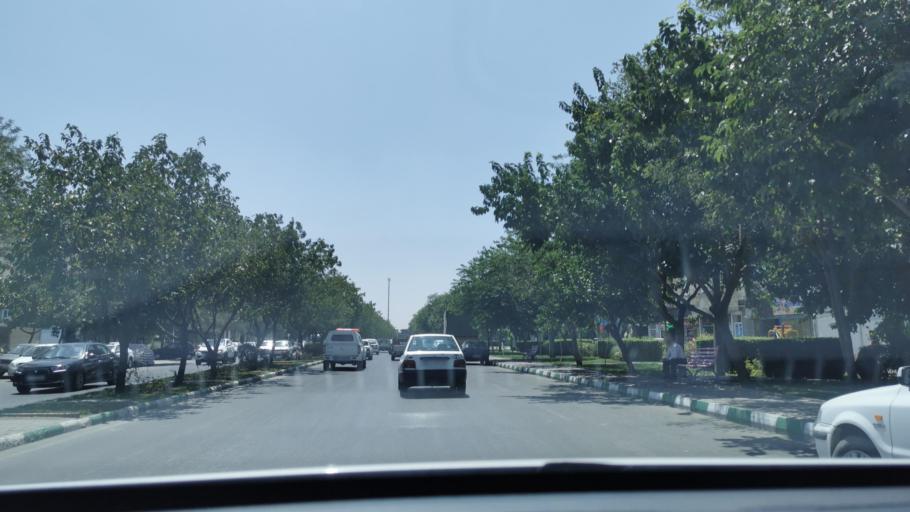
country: IR
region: Razavi Khorasan
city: Mashhad
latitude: 36.3457
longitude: 59.6264
